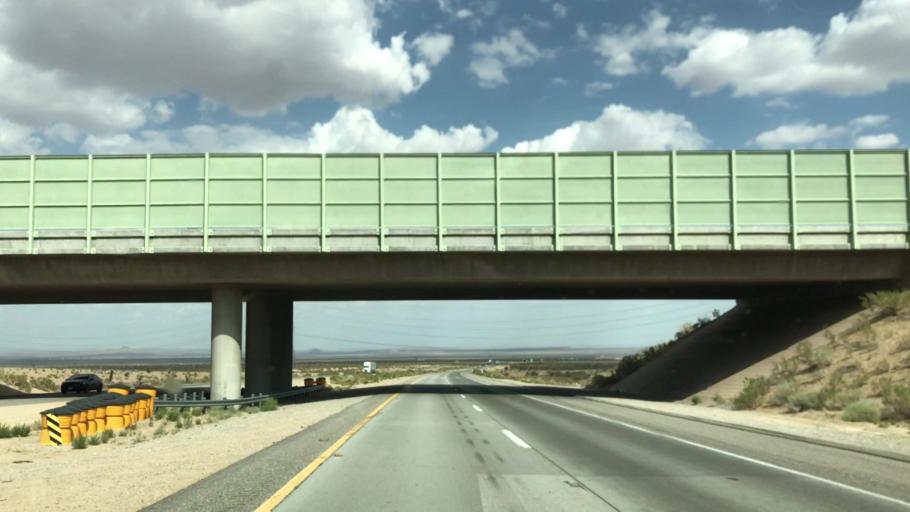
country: US
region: California
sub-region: Kern County
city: Mojave
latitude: 35.1137
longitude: -118.1790
